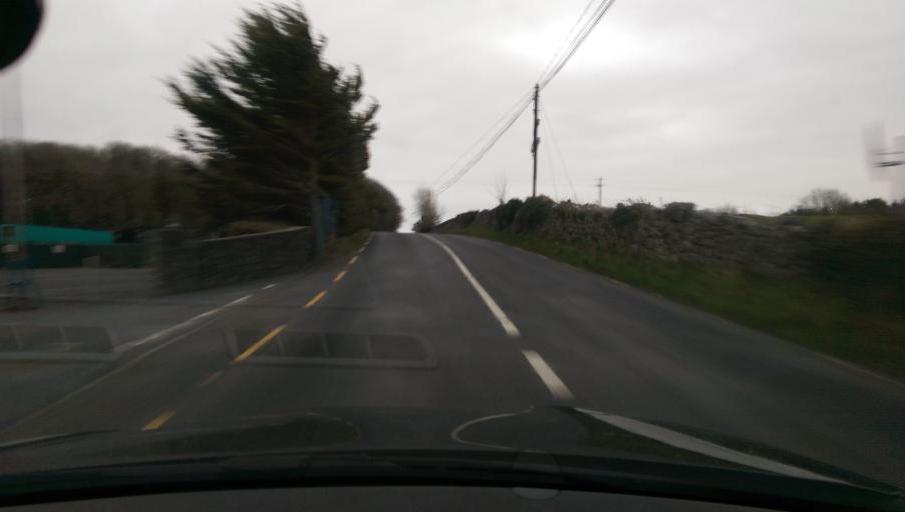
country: IE
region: Connaught
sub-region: County Galway
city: Athenry
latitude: 53.3087
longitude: -8.7916
